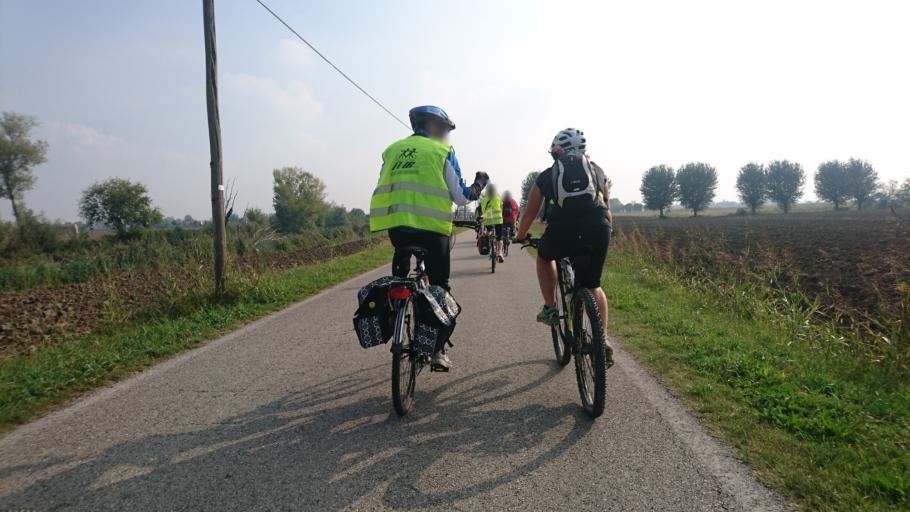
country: IT
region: Veneto
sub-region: Provincia di Rovigo
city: Bosaro
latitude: 44.9893
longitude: 11.7515
